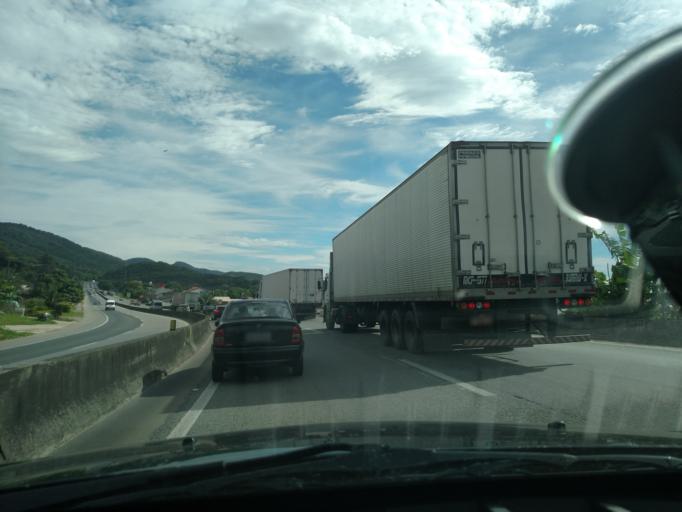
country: BR
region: Santa Catarina
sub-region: Biguacu
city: Biguacu
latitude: -27.4766
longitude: -48.6408
